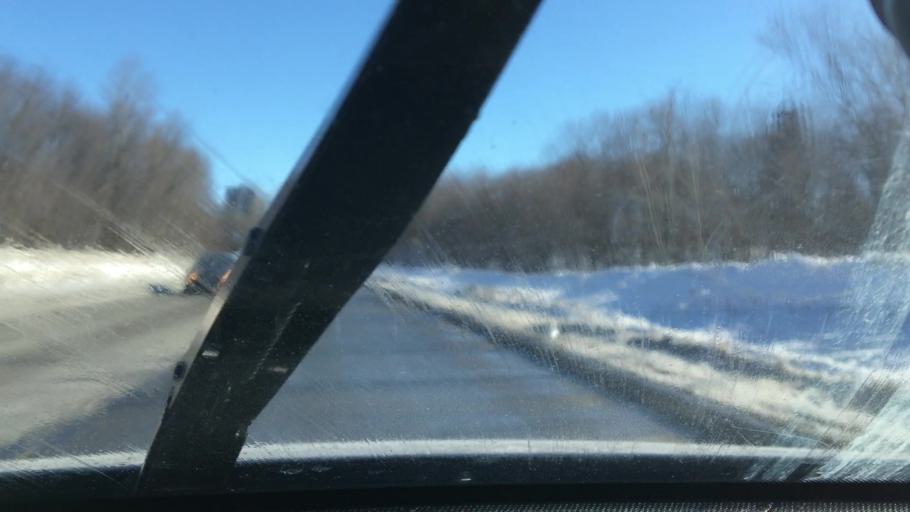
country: CA
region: Quebec
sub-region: Outaouais
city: Gatineau
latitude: 45.4491
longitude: -75.6461
